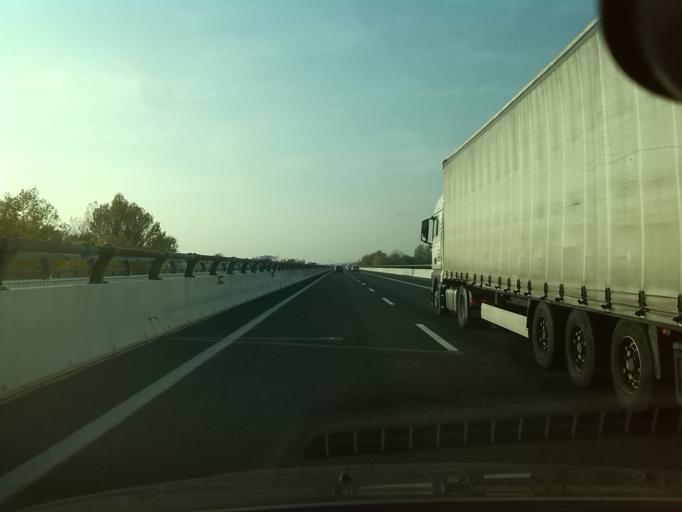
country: IT
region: Friuli Venezia Giulia
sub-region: Provincia di Gorizia
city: San Pier d'Isonzo
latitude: 45.8526
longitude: 13.4567
